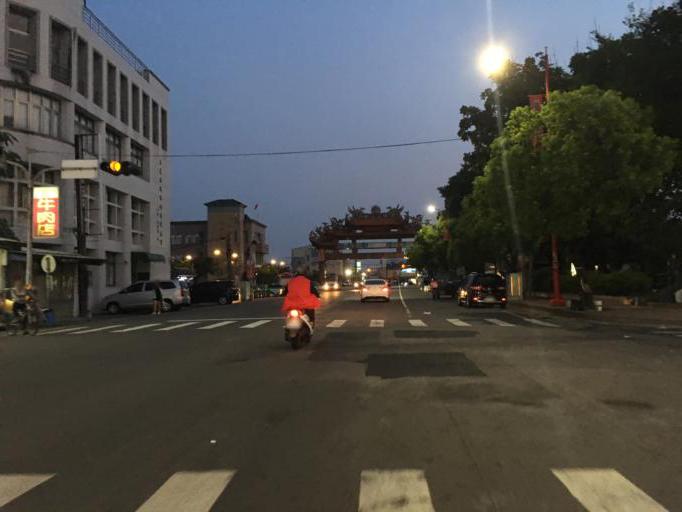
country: TW
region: Taiwan
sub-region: Chiayi
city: Taibao
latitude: 23.5527
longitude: 120.3474
